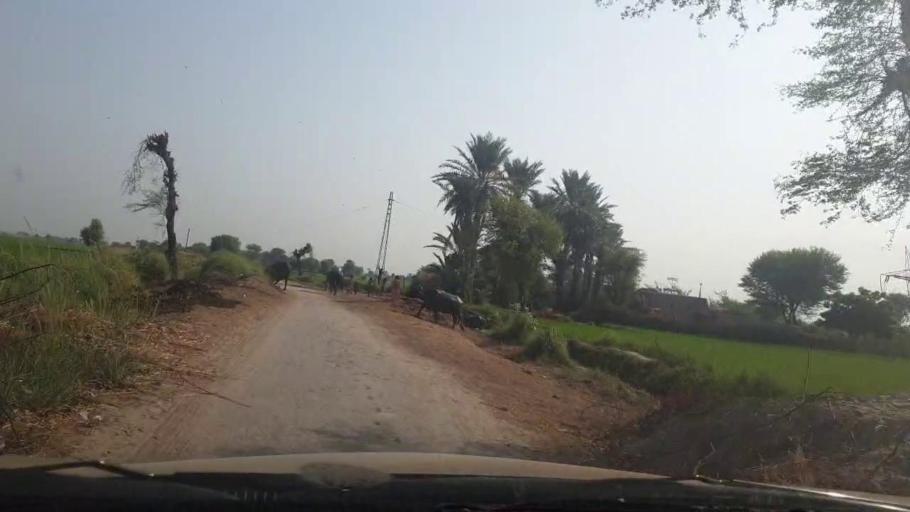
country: PK
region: Sindh
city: Larkana
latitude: 27.5835
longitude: 68.1863
